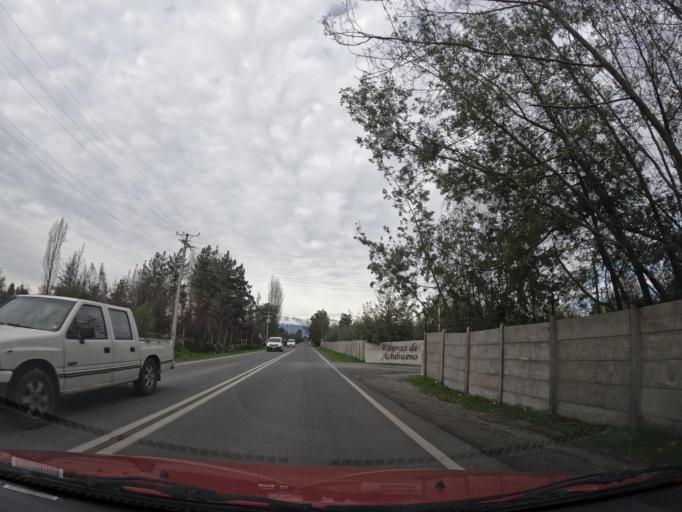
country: CL
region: Maule
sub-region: Provincia de Linares
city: Linares
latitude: -35.9043
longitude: -71.5075
